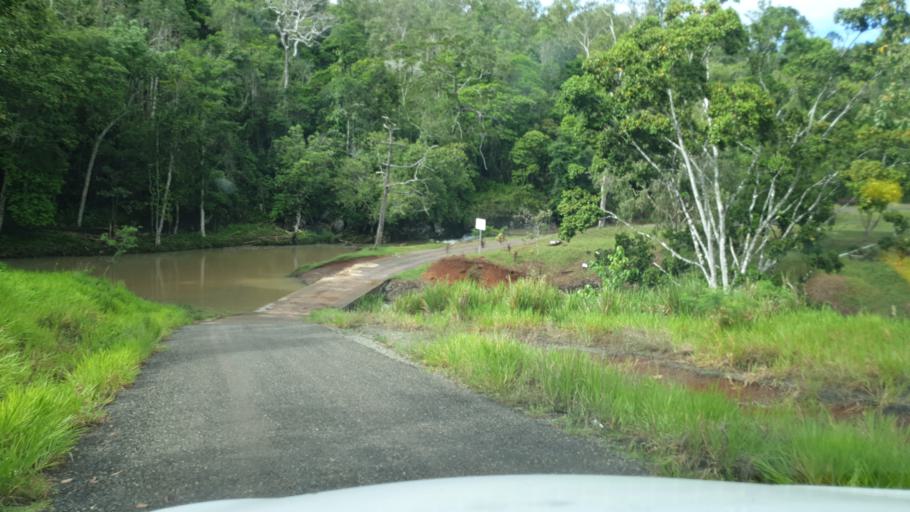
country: PG
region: National Capital
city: Port Moresby
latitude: -9.4356
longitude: 147.3943
